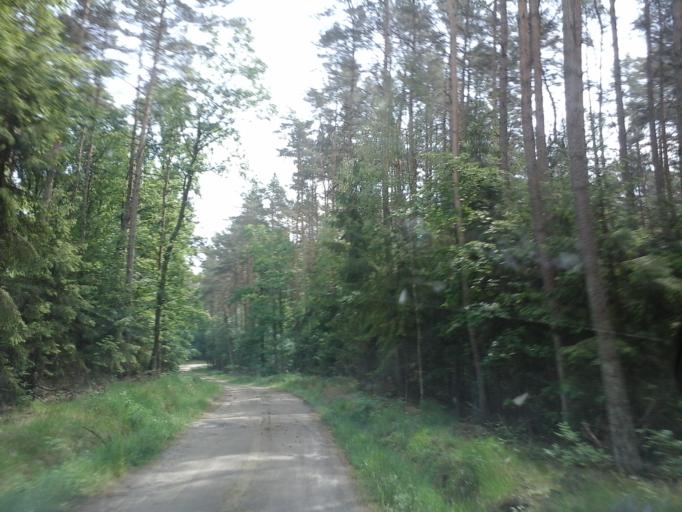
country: PL
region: West Pomeranian Voivodeship
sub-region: Powiat choszczenski
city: Drawno
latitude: 53.1942
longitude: 15.7612
